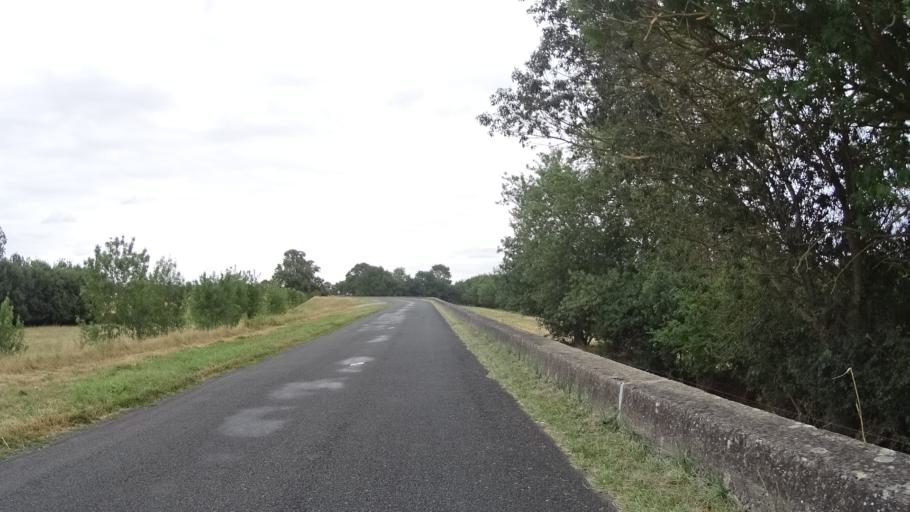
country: FR
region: Pays de la Loire
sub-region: Departement de Maine-et-Loire
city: La Possonniere
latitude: 47.3655
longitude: -0.7047
